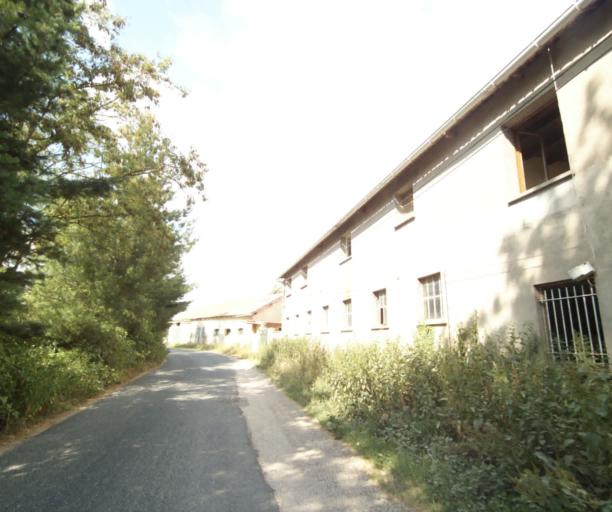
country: FR
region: Lorraine
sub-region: Departement de Meurthe-et-Moselle
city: Chanteheux
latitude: 48.5802
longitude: 6.5376
